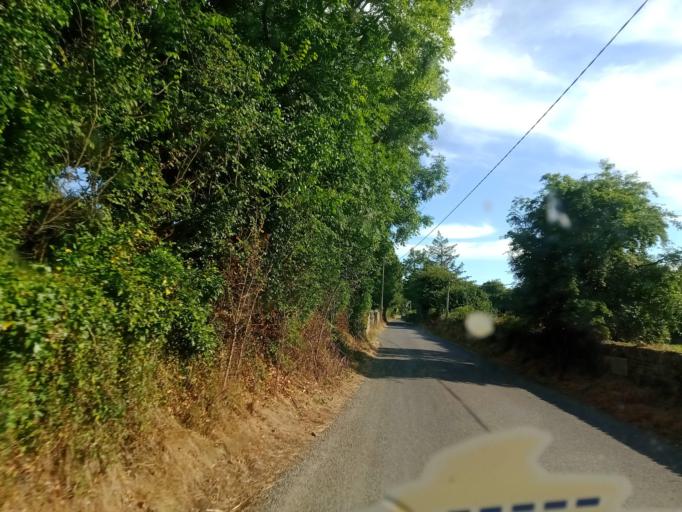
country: IE
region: Leinster
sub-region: Kilkenny
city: Ballyragget
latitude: 52.7802
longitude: -7.3907
